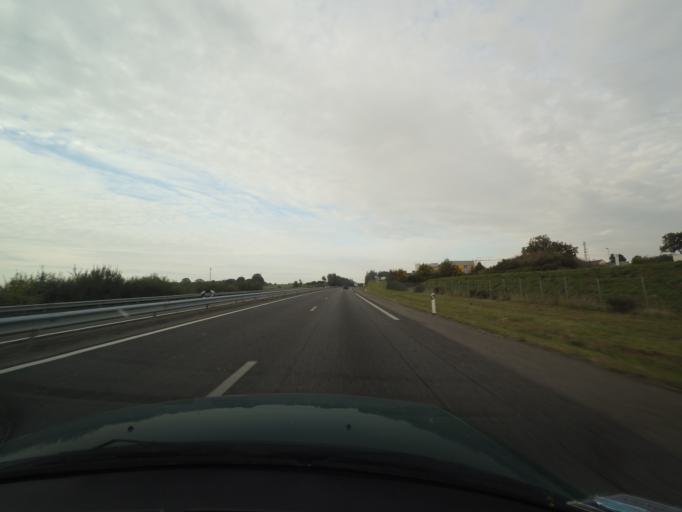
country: FR
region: Brittany
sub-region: Departement d'Ille-et-Vilaine
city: Bain-de-Bretagne
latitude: 47.8395
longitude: -1.6957
